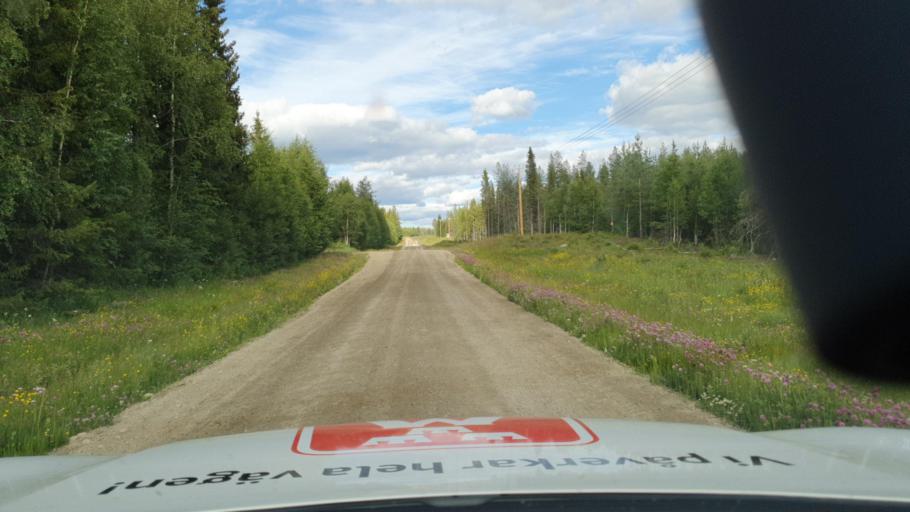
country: SE
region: Vaesterbotten
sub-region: Lycksele Kommun
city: Soderfors
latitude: 64.2943
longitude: 18.1963
